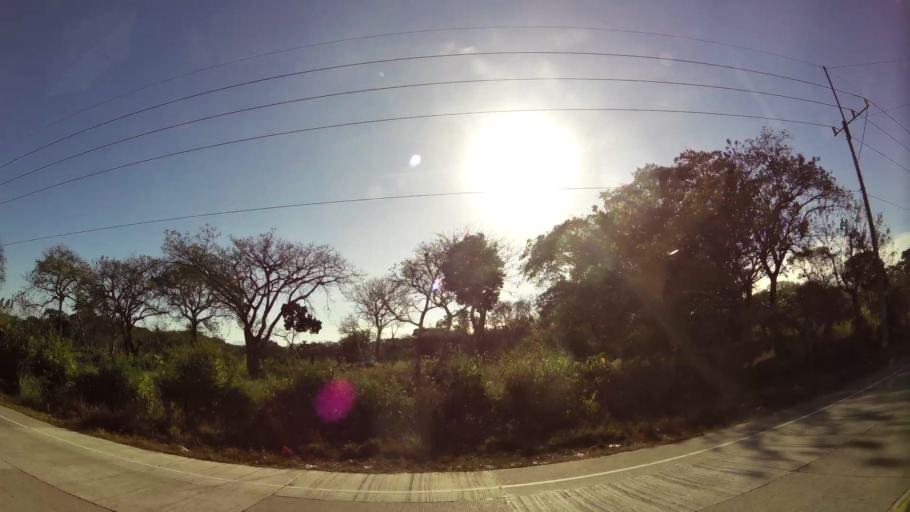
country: SV
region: Santa Ana
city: Metapan
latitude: 14.2366
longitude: -89.4691
